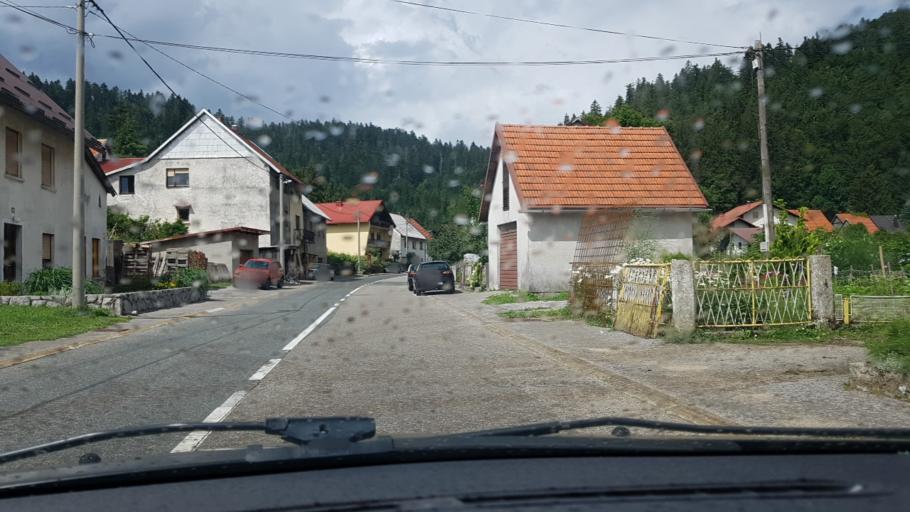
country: HR
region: Primorsko-Goranska
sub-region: Grad Delnice
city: Delnice
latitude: 45.3612
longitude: 14.7533
